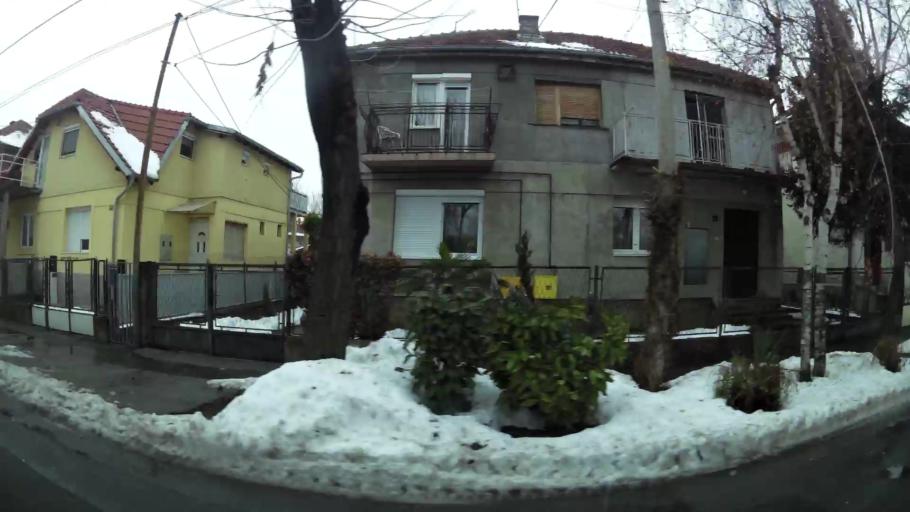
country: RS
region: Central Serbia
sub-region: Belgrade
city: Zemun
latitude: 44.8350
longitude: 20.3924
